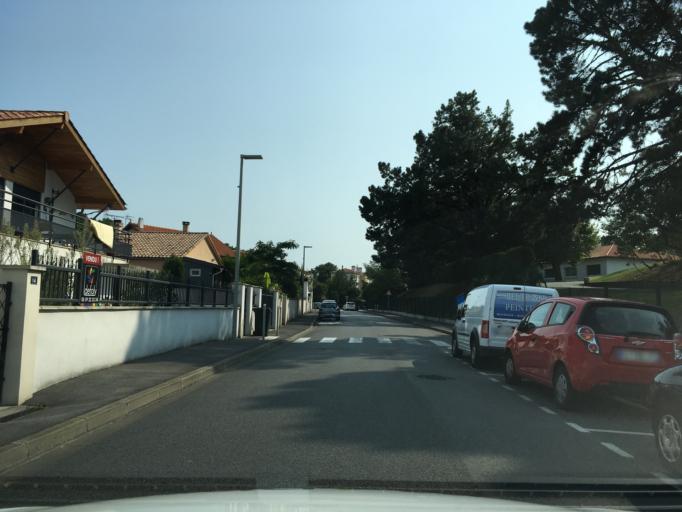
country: FR
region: Aquitaine
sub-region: Departement des Pyrenees-Atlantiques
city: Bayonne
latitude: 43.5083
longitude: -1.5025
